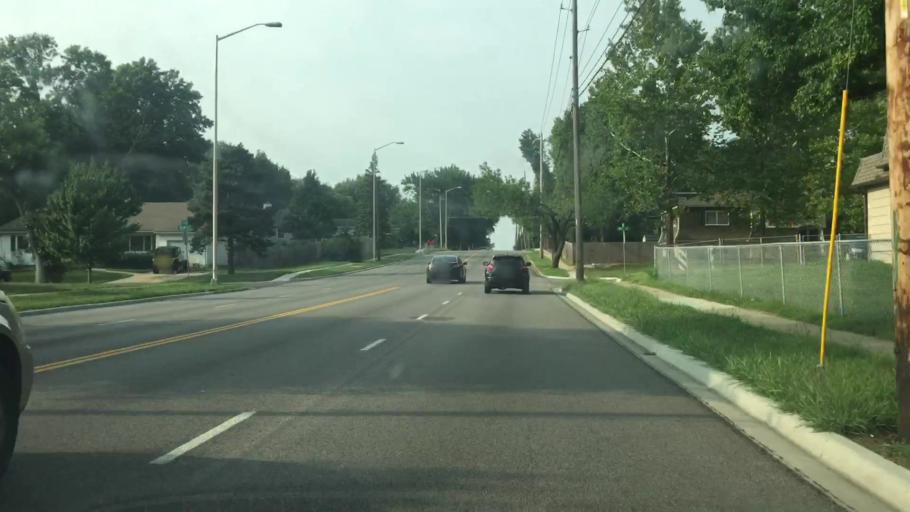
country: US
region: Kansas
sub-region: Johnson County
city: Overland Park
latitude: 38.9659
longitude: -94.6863
